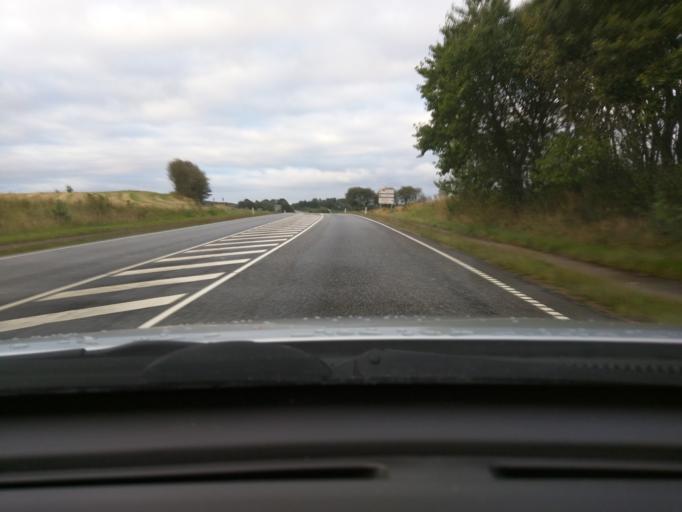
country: DK
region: Central Jutland
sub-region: Silkeborg Kommune
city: Kjellerup
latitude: 56.3478
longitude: 9.3534
